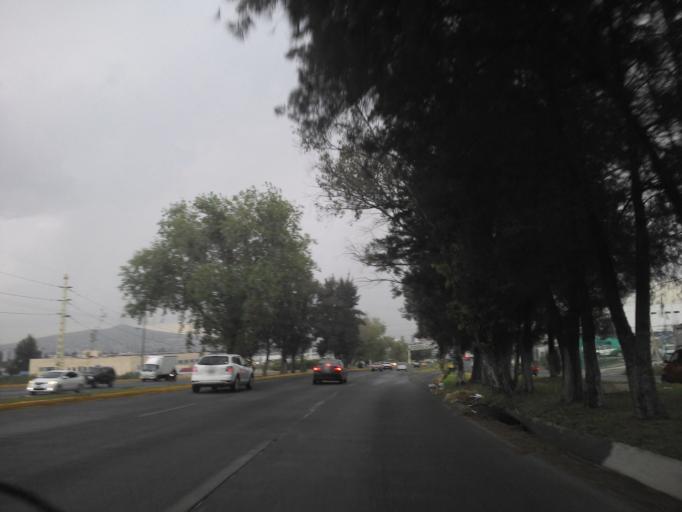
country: MX
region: Jalisco
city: Tlaquepaque
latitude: 20.6236
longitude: -103.3115
